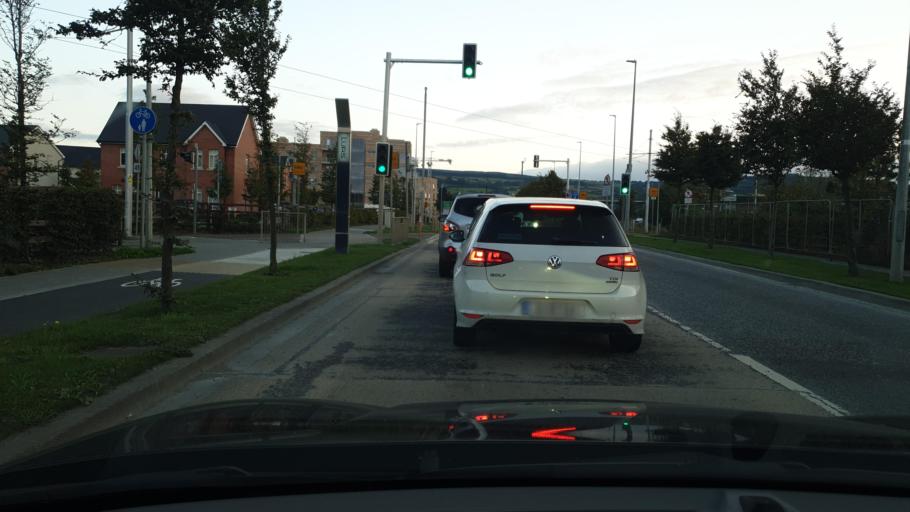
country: IE
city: Jobstown
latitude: 53.2859
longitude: -6.4218
